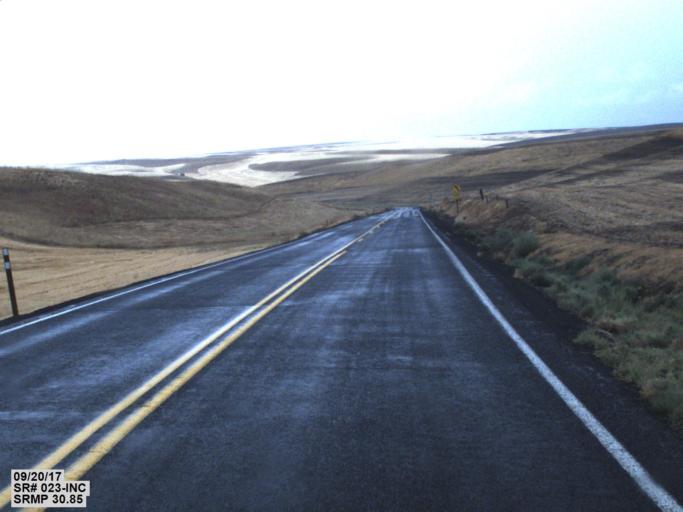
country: US
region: Washington
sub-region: Spokane County
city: Cheney
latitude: 47.1559
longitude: -117.8610
